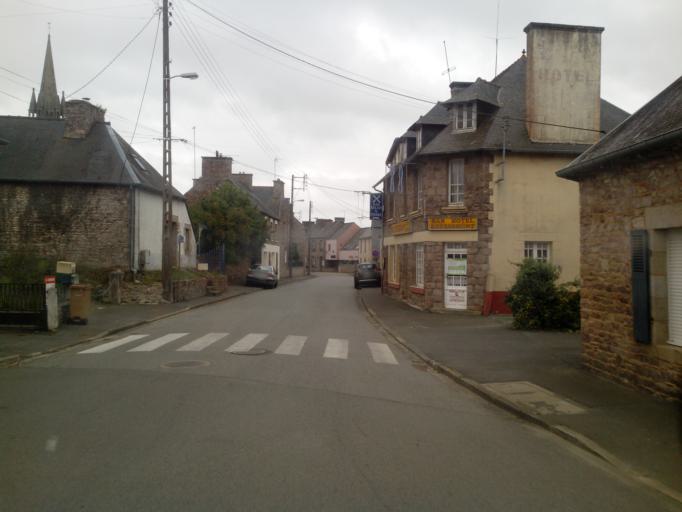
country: FR
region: Brittany
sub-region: Departement des Cotes-d'Armor
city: Plehedel
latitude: 48.6974
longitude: -3.0096
